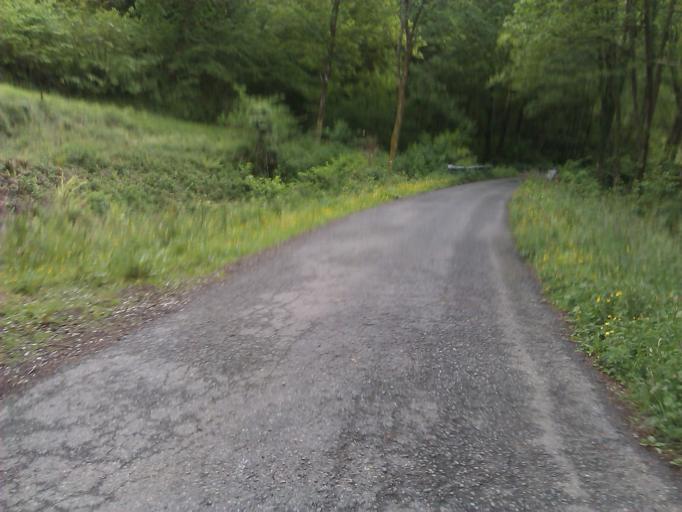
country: ES
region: Navarre
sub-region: Provincia de Navarra
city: Areso
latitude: 43.1058
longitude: -1.9374
